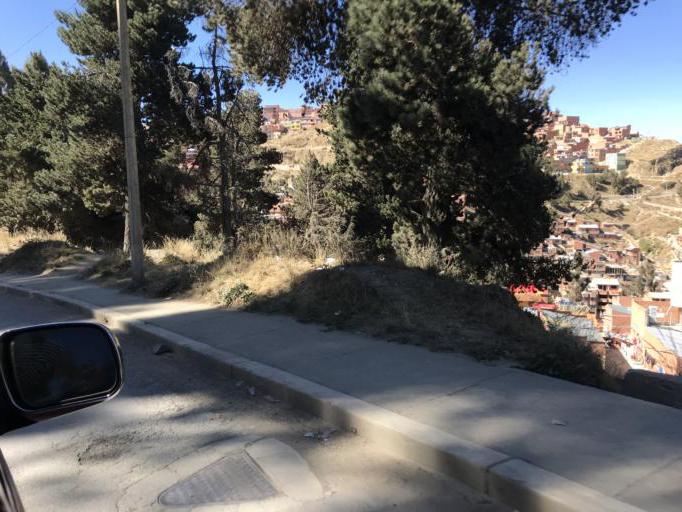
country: BO
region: La Paz
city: La Paz
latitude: -16.4854
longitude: -68.1684
